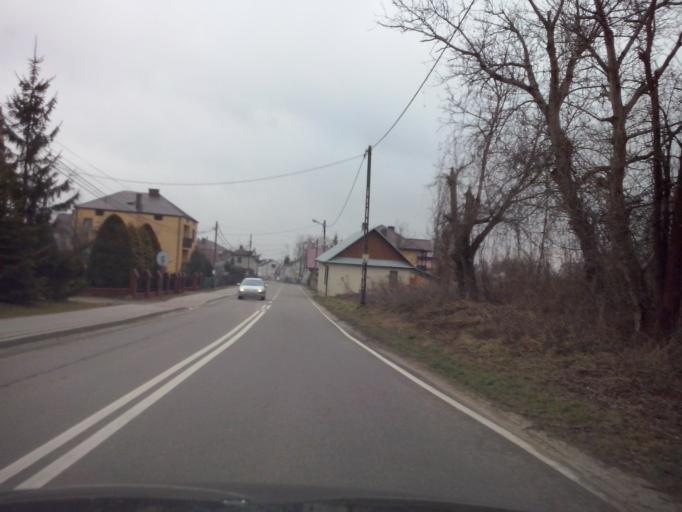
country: PL
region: Subcarpathian Voivodeship
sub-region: Powiat nizanski
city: Krzeszow
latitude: 50.4058
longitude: 22.3411
